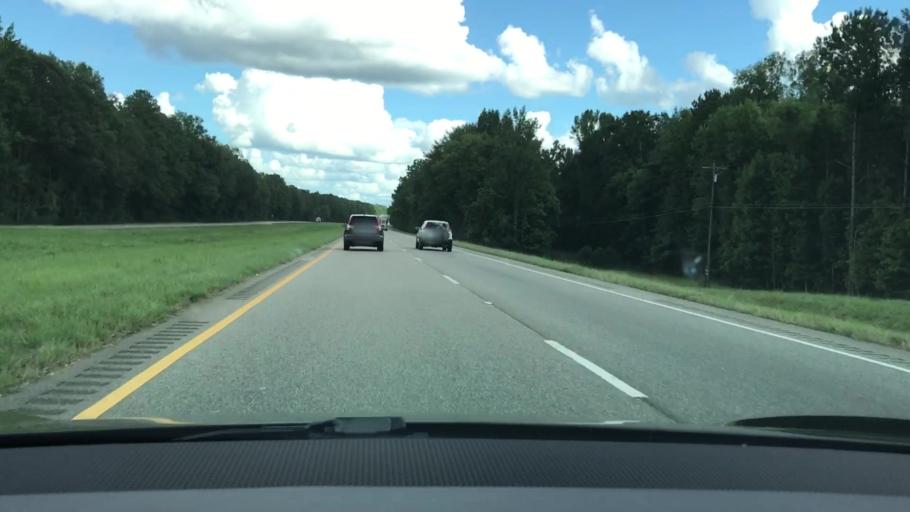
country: US
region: Alabama
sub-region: Montgomery County
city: Pike Road
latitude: 32.1394
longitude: -86.0946
